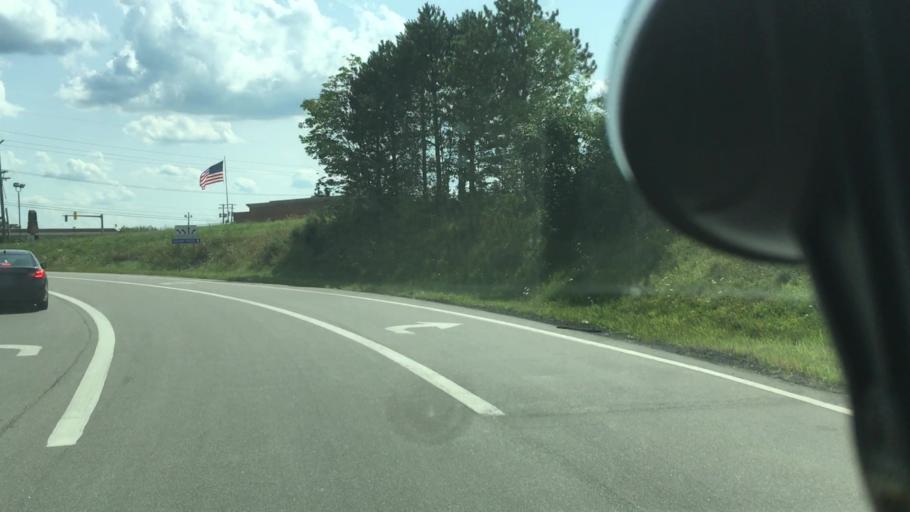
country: US
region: Ohio
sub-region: Mahoning County
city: Canfield
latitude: 41.0260
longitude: -80.7418
